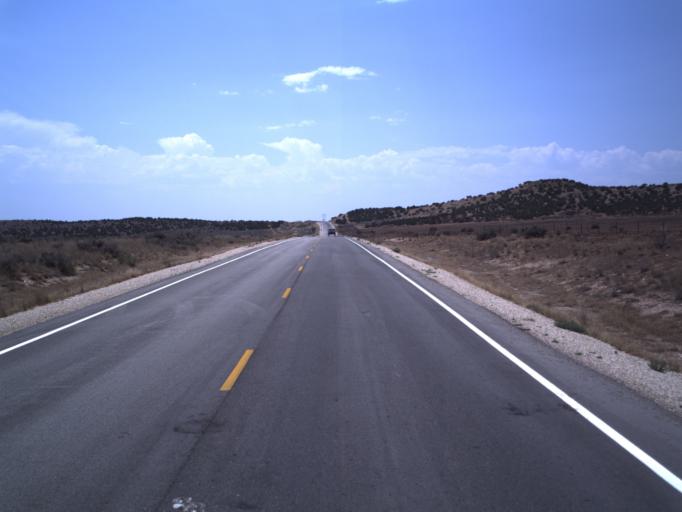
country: US
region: Utah
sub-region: Uintah County
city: Maeser
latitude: 40.4461
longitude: -109.6324
